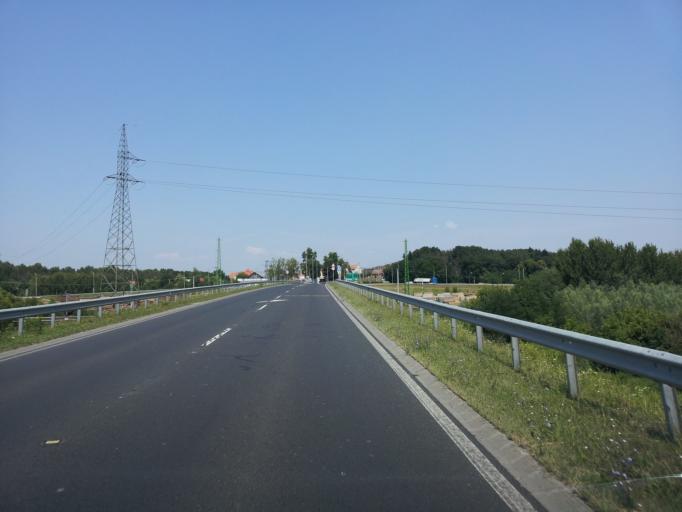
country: HU
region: Zala
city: Zalaegerszeg
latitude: 46.8595
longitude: 16.8560
